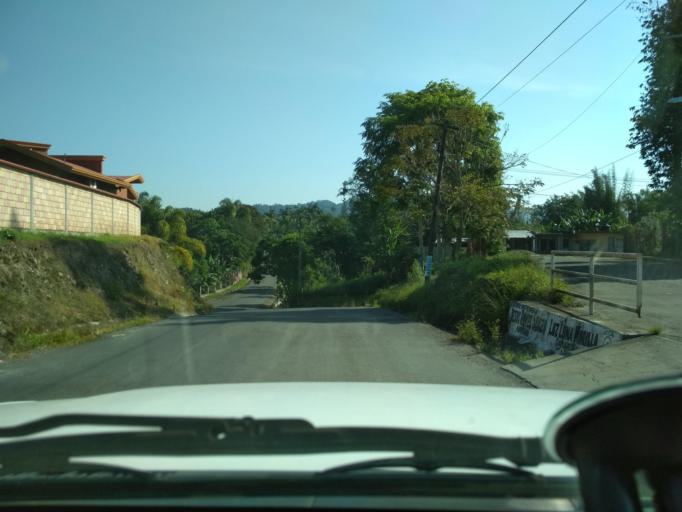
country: MX
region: Veracruz
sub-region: Chocaman
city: San Jose Neria
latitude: 18.9952
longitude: -97.0021
